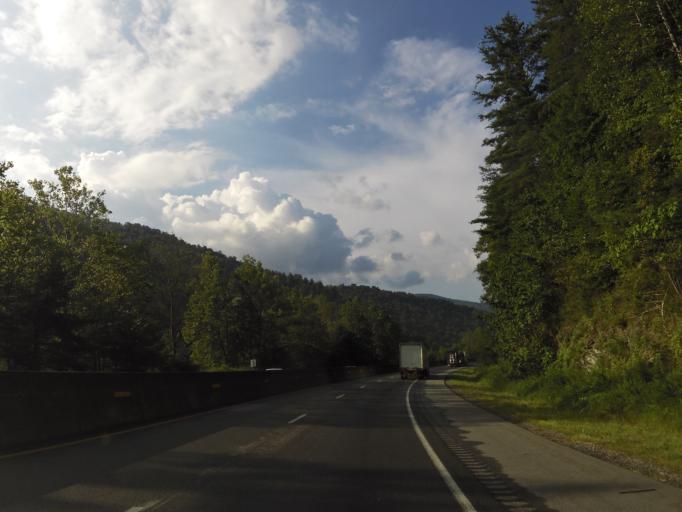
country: US
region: North Carolina
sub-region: Haywood County
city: Cove Creek
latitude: 35.7408
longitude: -83.0360
